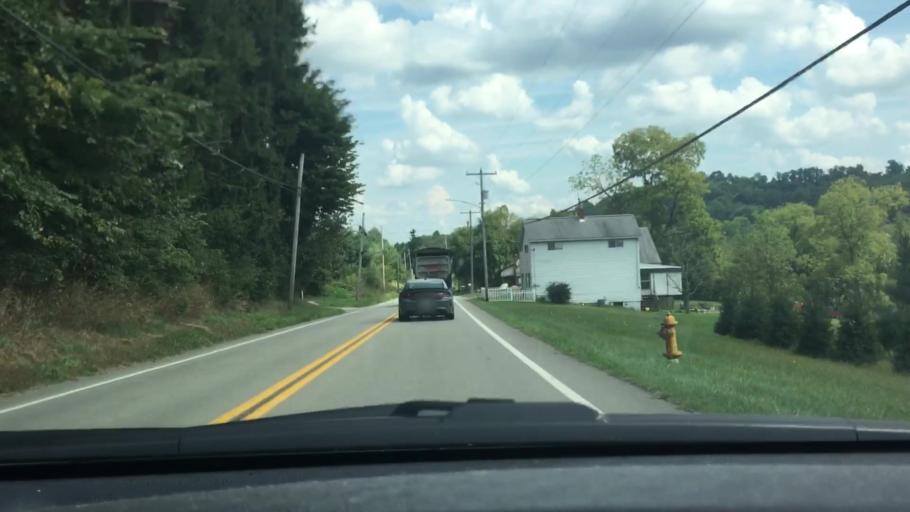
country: US
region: Pennsylvania
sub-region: Washington County
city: McMurray
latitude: 40.2453
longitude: -80.0527
